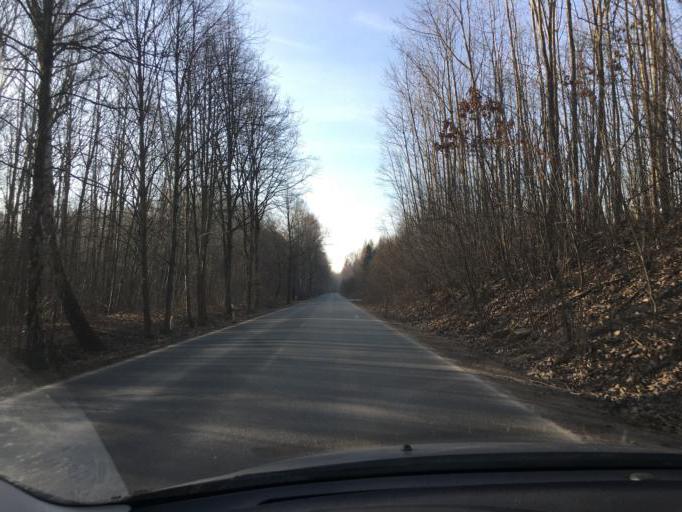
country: DE
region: Thuringia
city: Nobitz
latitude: 50.9669
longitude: 12.5145
